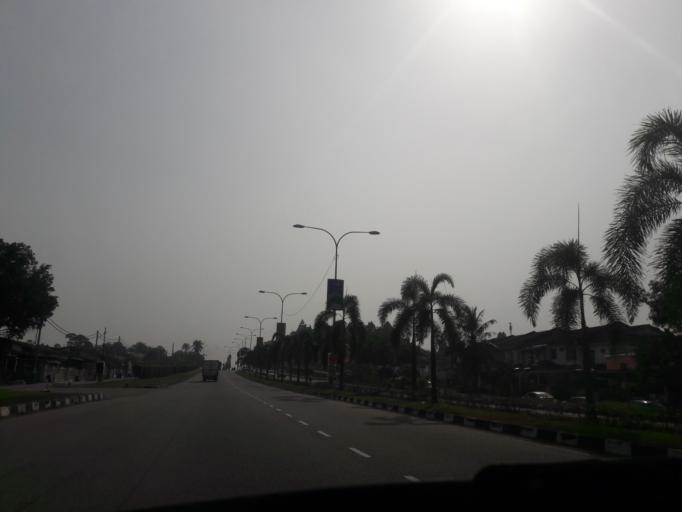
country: MY
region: Kedah
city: Kulim
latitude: 5.3576
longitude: 100.5426
